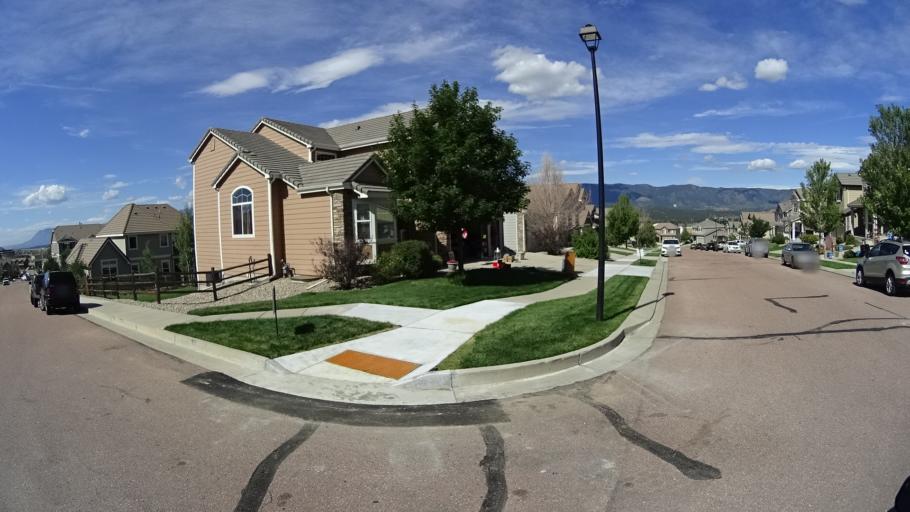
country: US
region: Colorado
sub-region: El Paso County
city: Gleneagle
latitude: 39.0266
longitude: -104.8112
